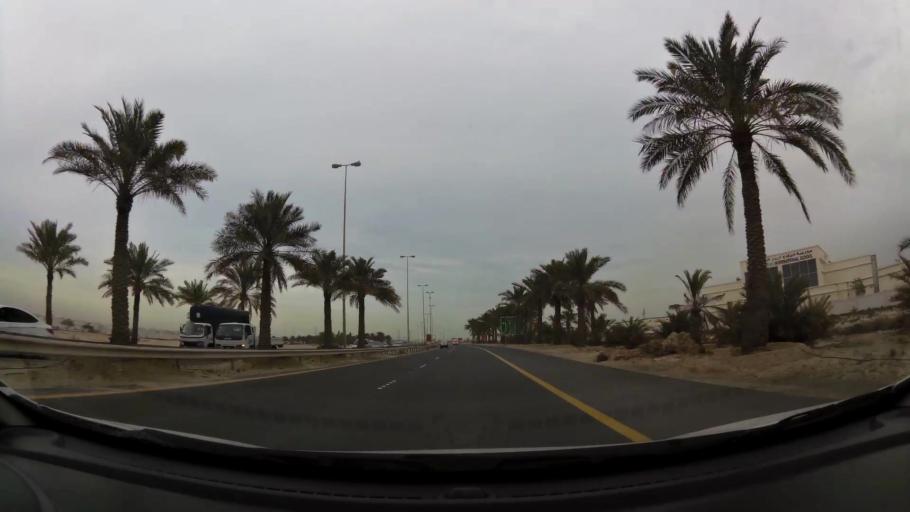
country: BH
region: Northern
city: Ar Rifa'
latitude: 26.1025
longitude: 50.5612
